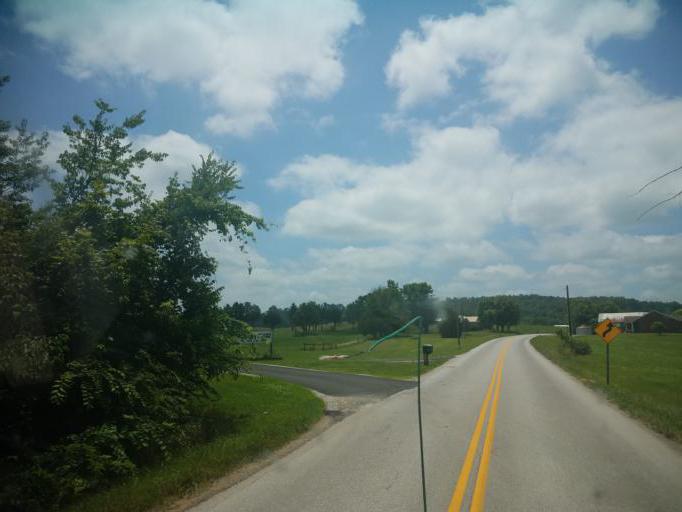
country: US
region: Kentucky
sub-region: Hart County
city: Munfordville
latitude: 37.3617
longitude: -86.0384
